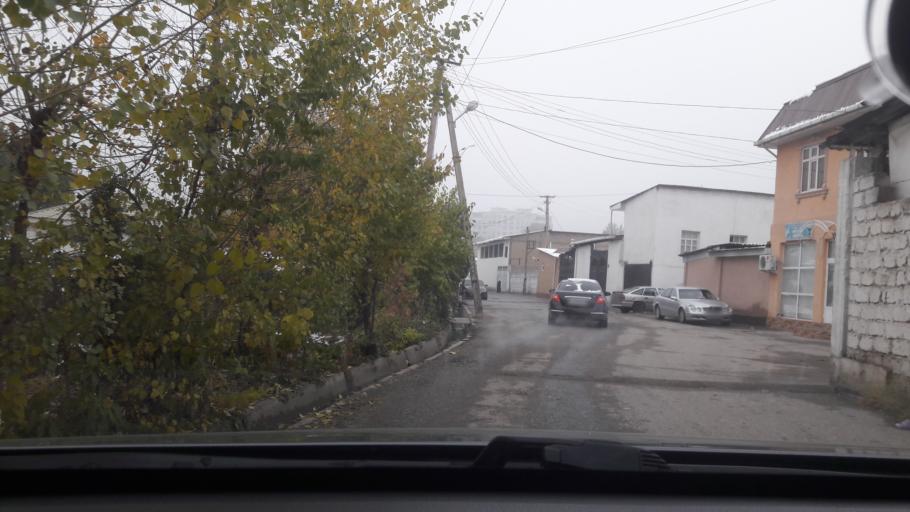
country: TJ
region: Dushanbe
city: Dushanbe
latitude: 38.5894
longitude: 68.7480
